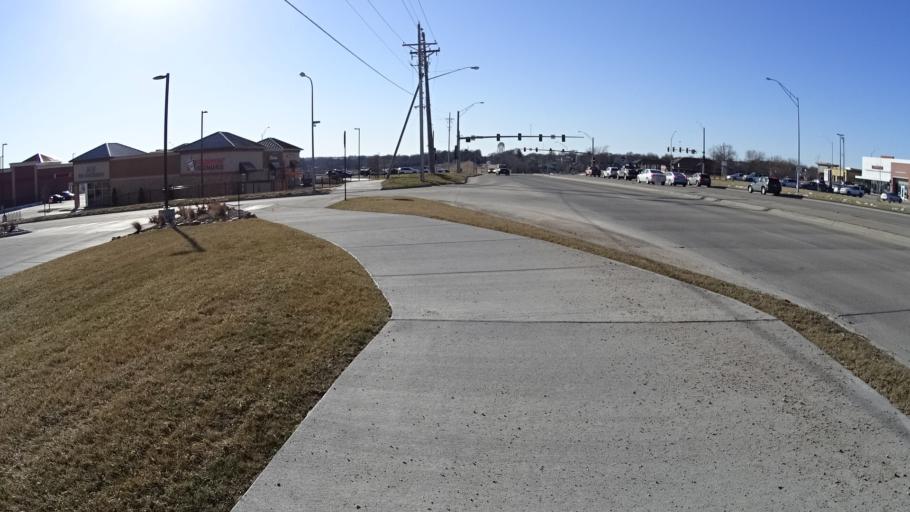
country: US
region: Nebraska
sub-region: Sarpy County
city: Papillion
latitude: 41.1615
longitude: -96.0222
